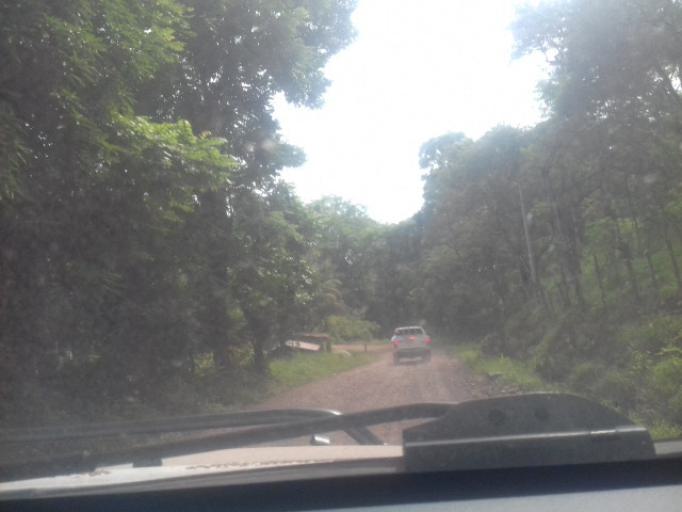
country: NI
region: Atlantico Norte (RAAN)
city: Waslala
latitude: 13.4392
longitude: -85.3081
